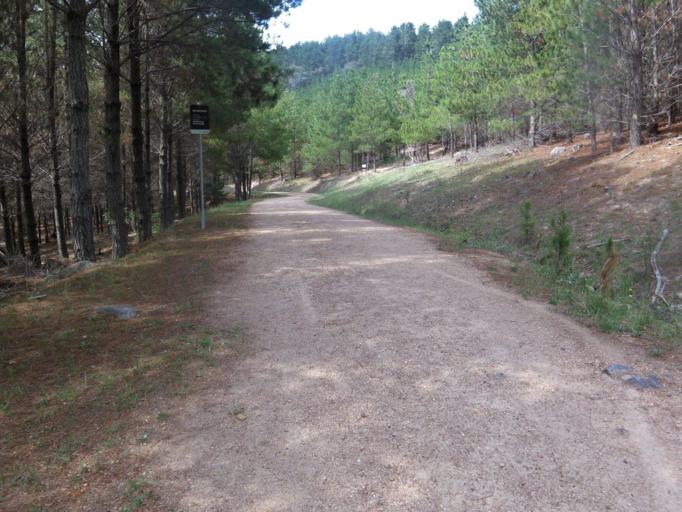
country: AU
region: Australian Capital Territory
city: Macarthur
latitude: -35.3818
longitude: 149.1210
